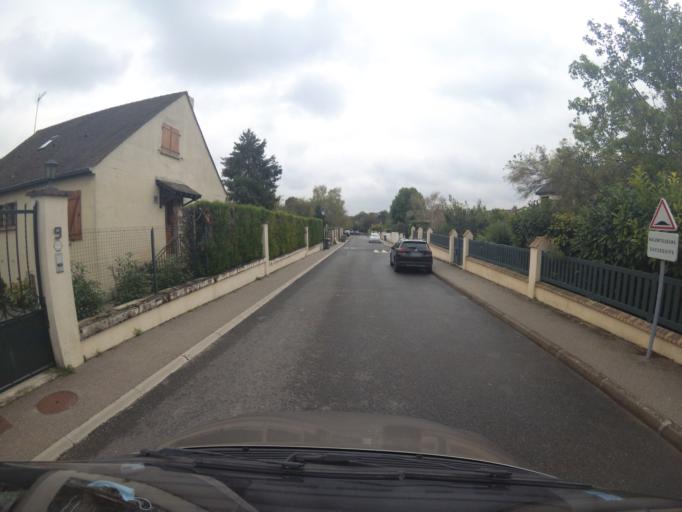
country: FR
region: Ile-de-France
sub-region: Departement de Seine-et-Marne
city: Gouvernes
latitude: 48.8491
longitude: 2.6909
